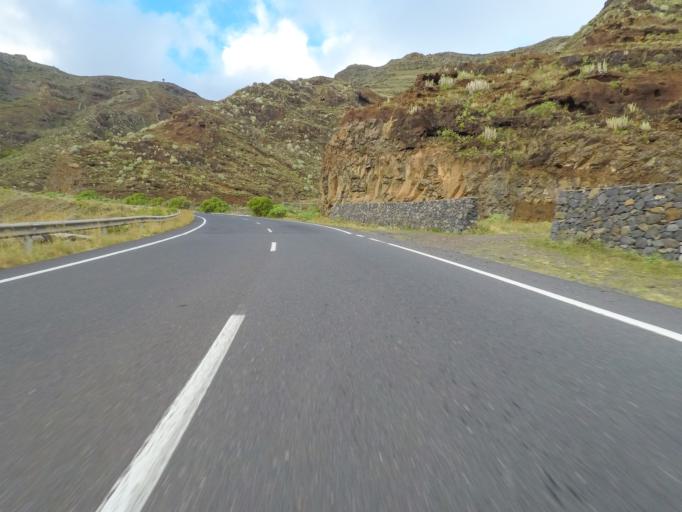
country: ES
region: Canary Islands
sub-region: Provincia de Santa Cruz de Tenerife
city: San Sebastian de la Gomera
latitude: 28.1228
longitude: -17.1454
